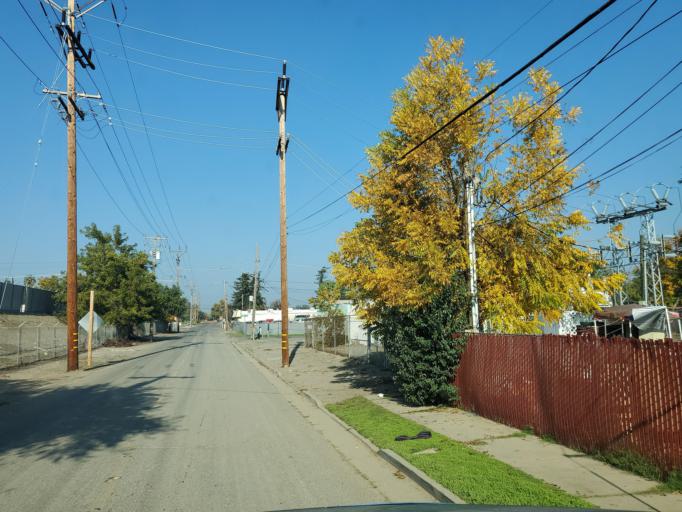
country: US
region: California
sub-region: San Joaquin County
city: Country Club
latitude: 37.9550
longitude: -121.3328
